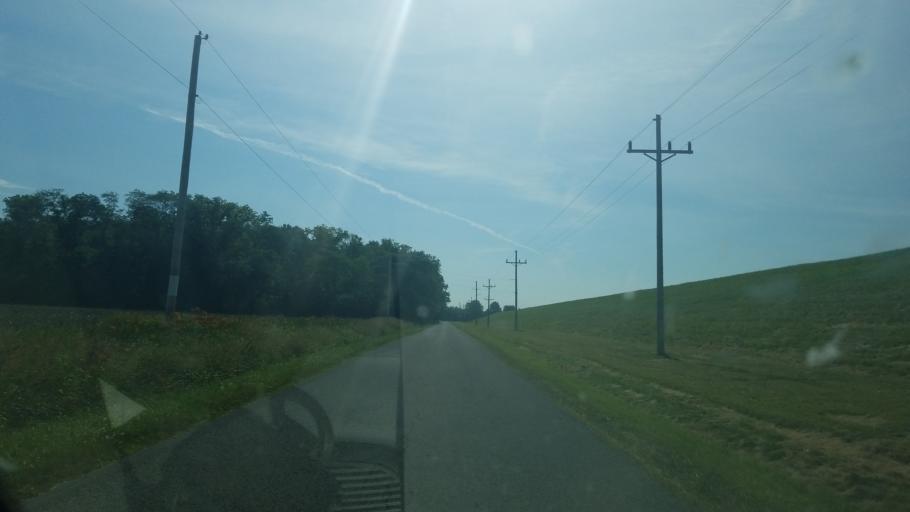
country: US
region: Ohio
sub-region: Hancock County
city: Findlay
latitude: 41.0289
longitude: -83.5729
